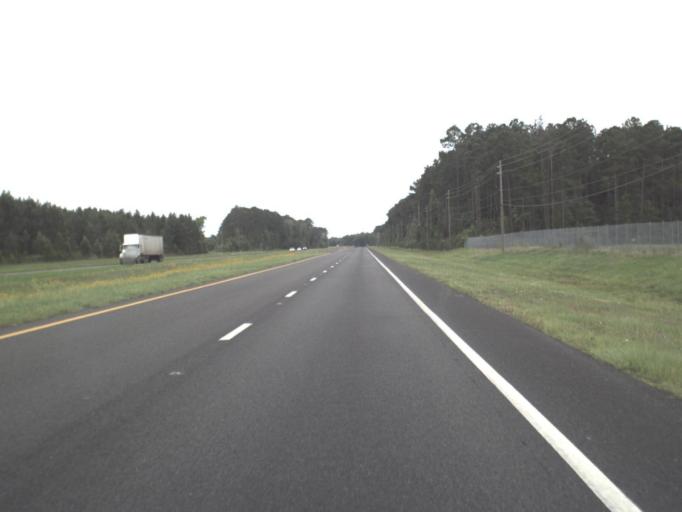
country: US
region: Florida
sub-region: Nassau County
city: Yulee
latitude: 30.6147
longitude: -81.6967
